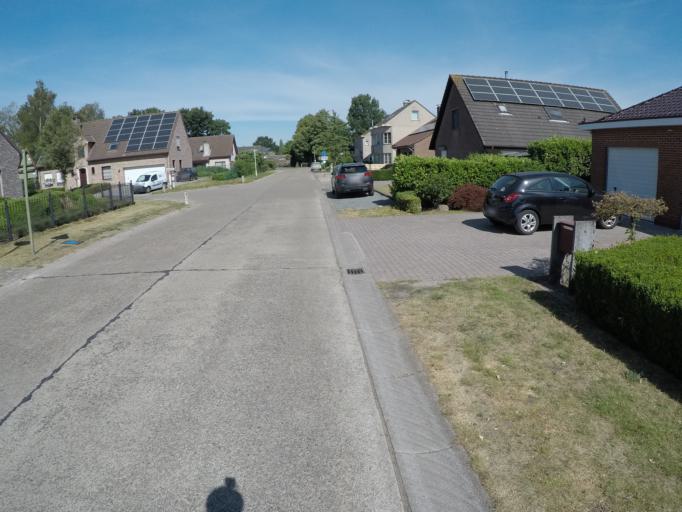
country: BE
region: Flanders
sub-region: Provincie Antwerpen
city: Wuustwezel
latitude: 51.3617
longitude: 4.5509
